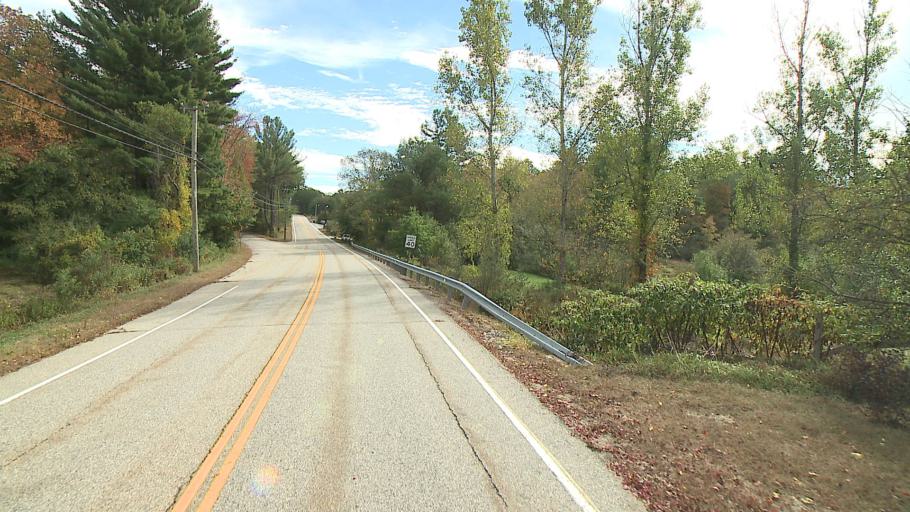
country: US
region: Connecticut
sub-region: Windham County
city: Putnam
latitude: 41.8986
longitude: -71.8871
